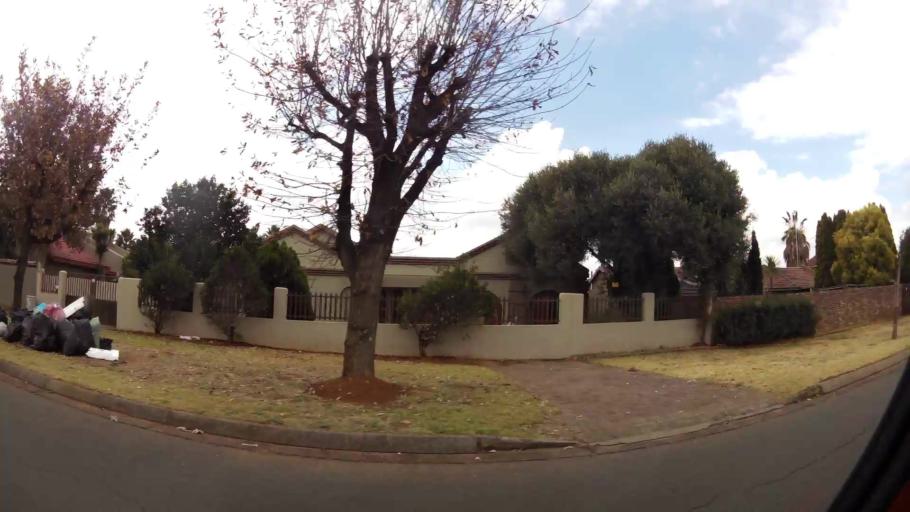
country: ZA
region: Gauteng
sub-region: Sedibeng District Municipality
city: Vanderbijlpark
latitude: -26.7354
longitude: 27.8547
